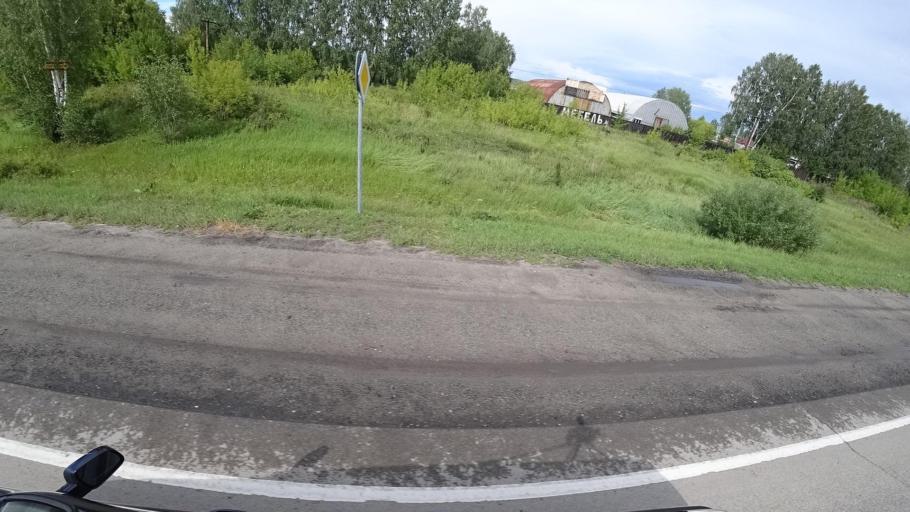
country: RU
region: Sverdlovsk
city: Kamyshlov
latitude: 56.8415
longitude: 62.7858
